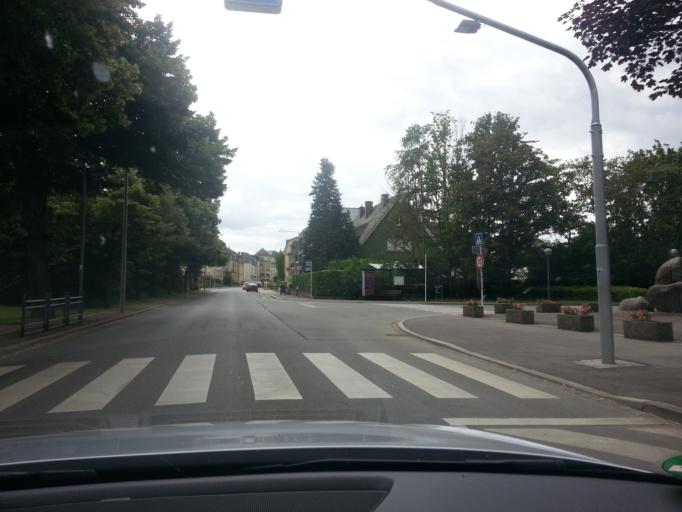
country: LU
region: Grevenmacher
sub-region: Canton de Remich
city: Mondorf-les-Bains
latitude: 49.5065
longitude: 6.2819
